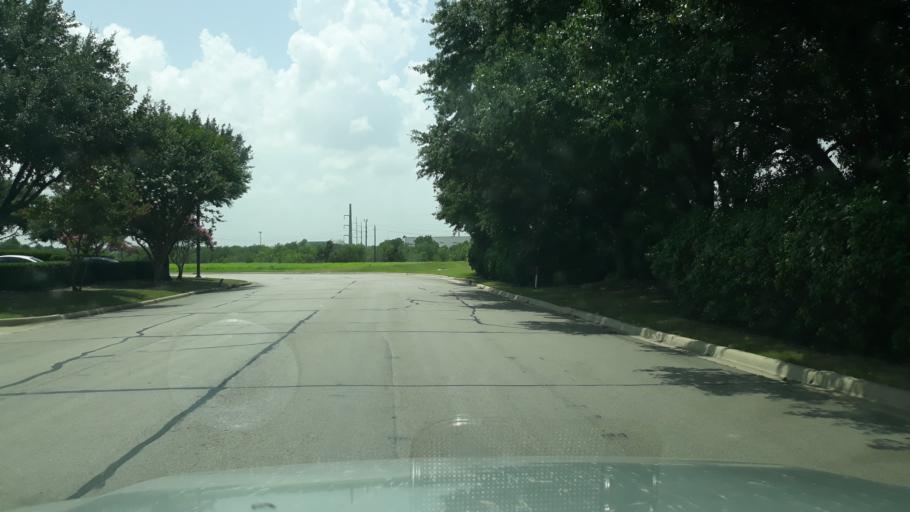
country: US
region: Texas
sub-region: Dallas County
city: Coppell
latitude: 32.9437
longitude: -97.0073
